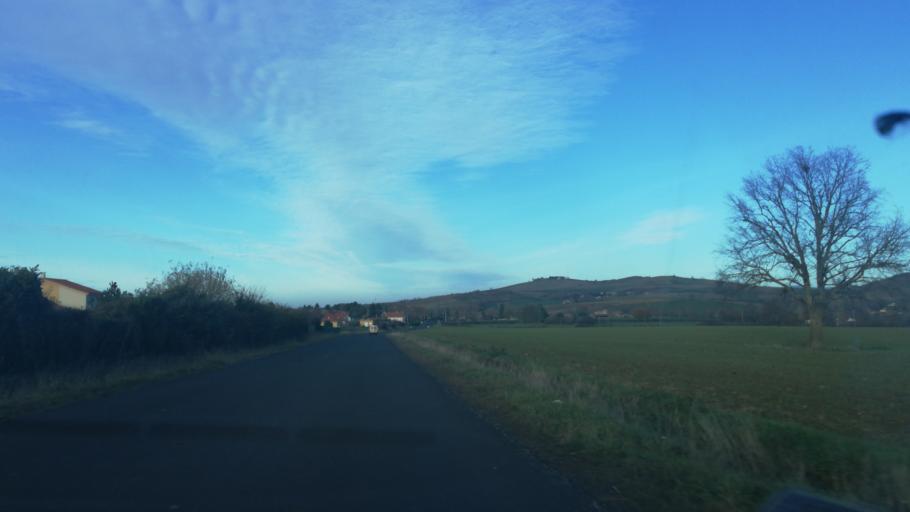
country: FR
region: Auvergne
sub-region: Departement du Puy-de-Dome
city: Billom
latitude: 45.7173
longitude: 3.3485
